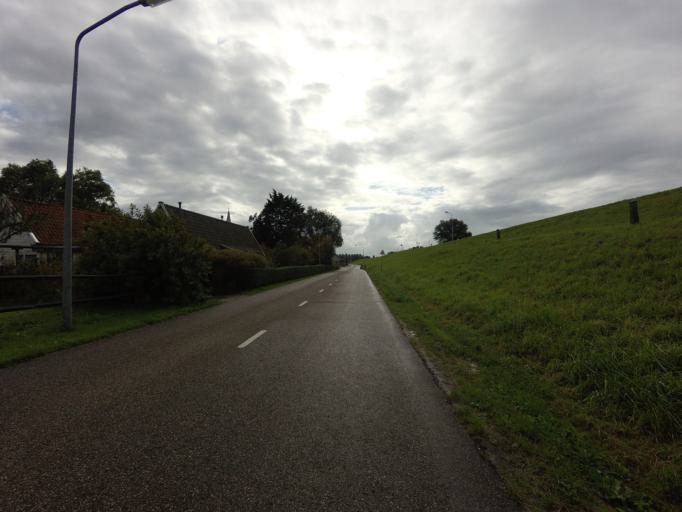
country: NL
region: North Holland
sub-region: Gemeente Enkhuizen
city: Enkhuizen
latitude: 52.7459
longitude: 5.2502
